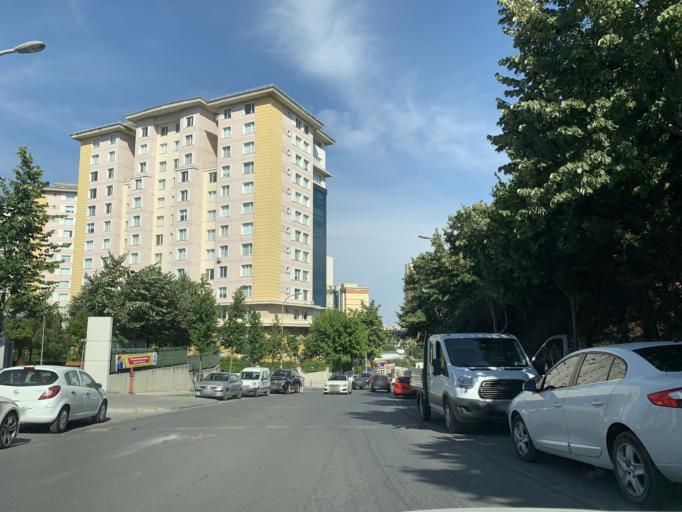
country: TR
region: Istanbul
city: Esenyurt
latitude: 41.0727
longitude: 28.6827
